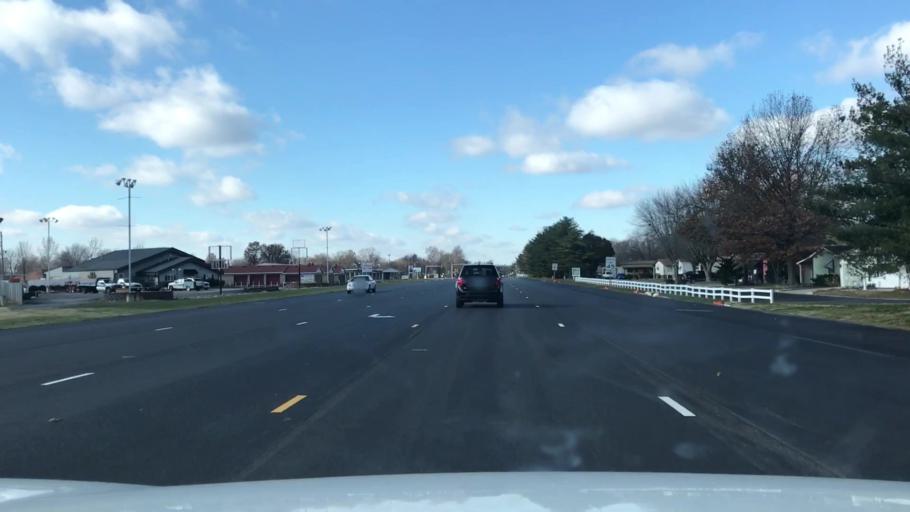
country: US
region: Illinois
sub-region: Saint Clair County
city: Swansea
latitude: 38.5488
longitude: -90.0069
